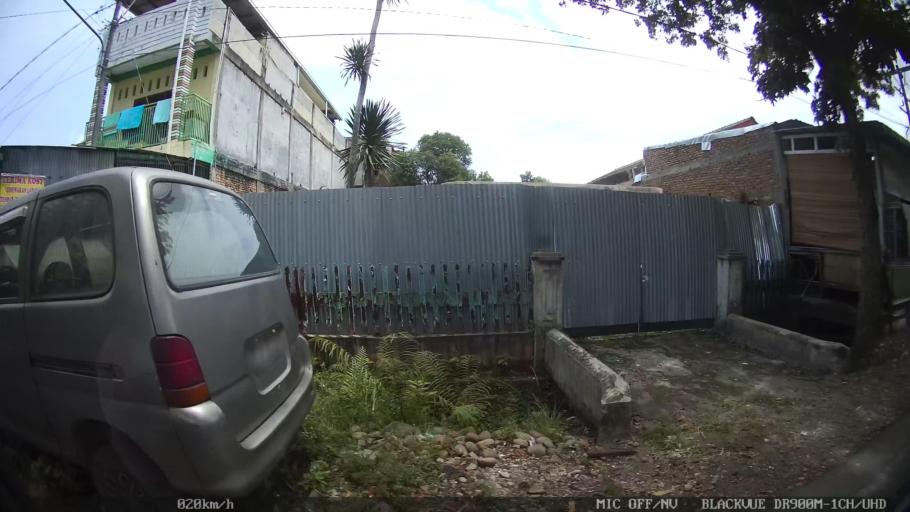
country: ID
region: North Sumatra
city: Medan
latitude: 3.5550
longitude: 98.6606
